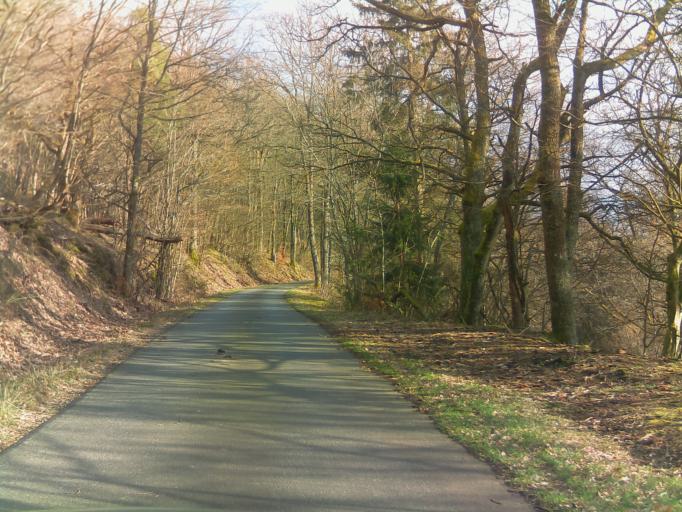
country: DE
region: Rheinland-Pfalz
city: Kronweiler
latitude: 49.6550
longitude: 7.2667
